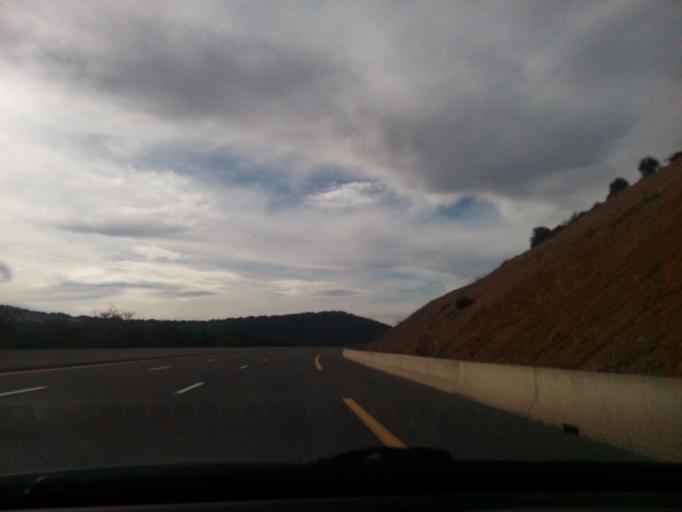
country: DZ
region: Sidi Bel Abbes
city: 'Ain el Berd
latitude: 35.3919
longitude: -0.4881
